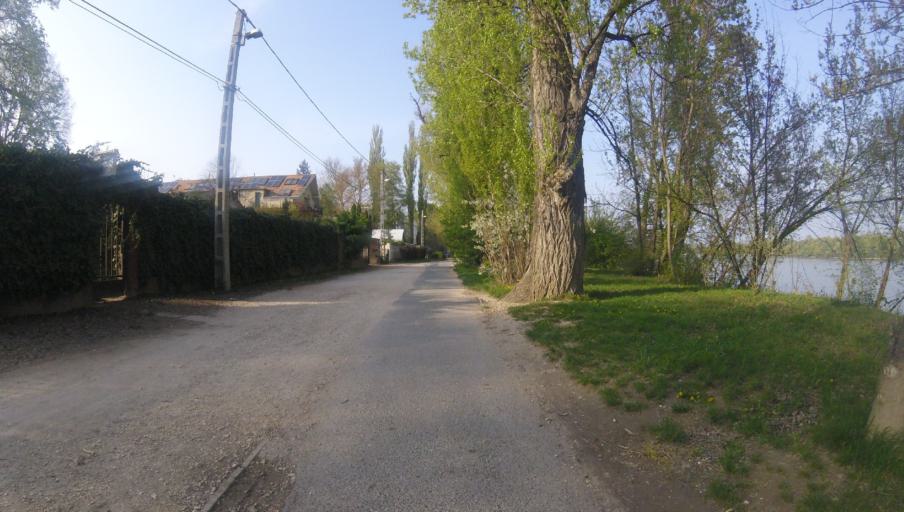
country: HU
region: Budapest
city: Budapest IV. keruelet
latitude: 47.5790
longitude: 19.0663
